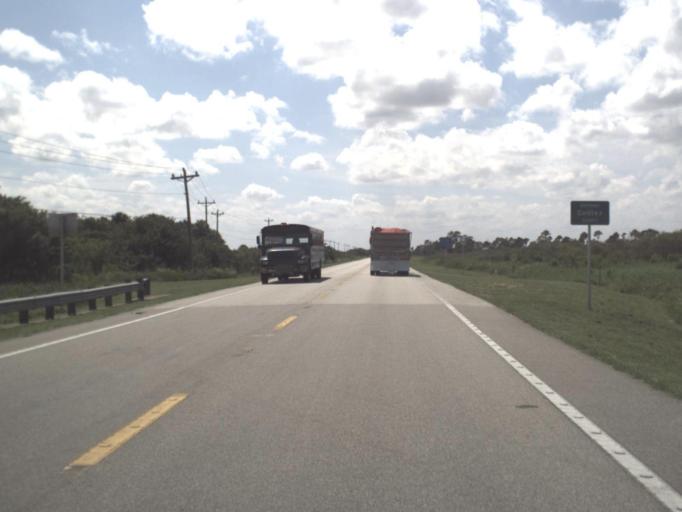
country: US
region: Florida
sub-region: Collier County
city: Immokalee
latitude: 26.5160
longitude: -81.4351
